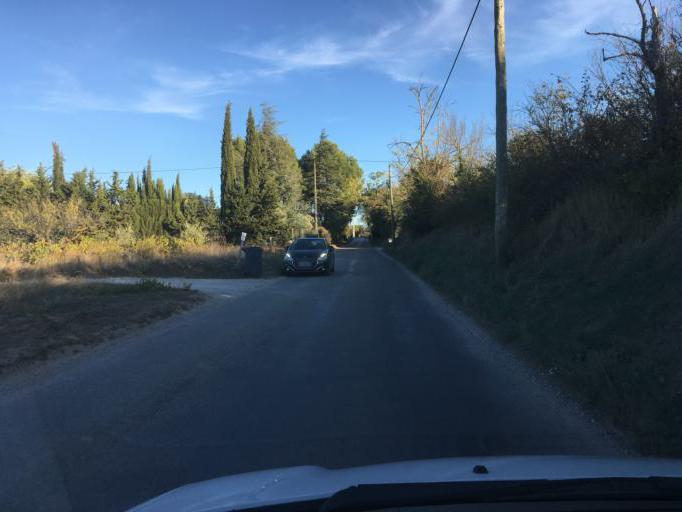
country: FR
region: Provence-Alpes-Cote d'Azur
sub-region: Departement du Vaucluse
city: Carpentras
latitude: 44.0587
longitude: 5.0771
